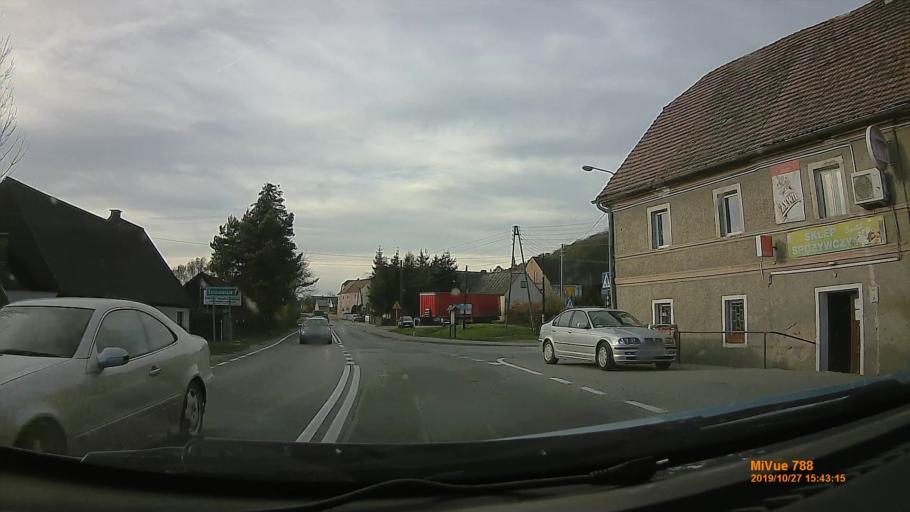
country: PL
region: Lower Silesian Voivodeship
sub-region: Powiat klodzki
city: Klodzko
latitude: 50.4675
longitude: 16.6213
